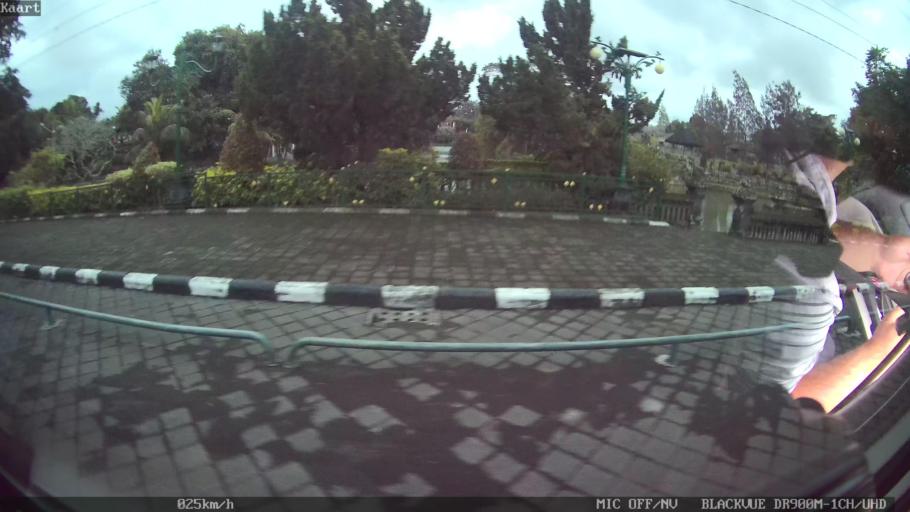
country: ID
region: Bali
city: Banjar Serangan
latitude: -8.5439
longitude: 115.1714
